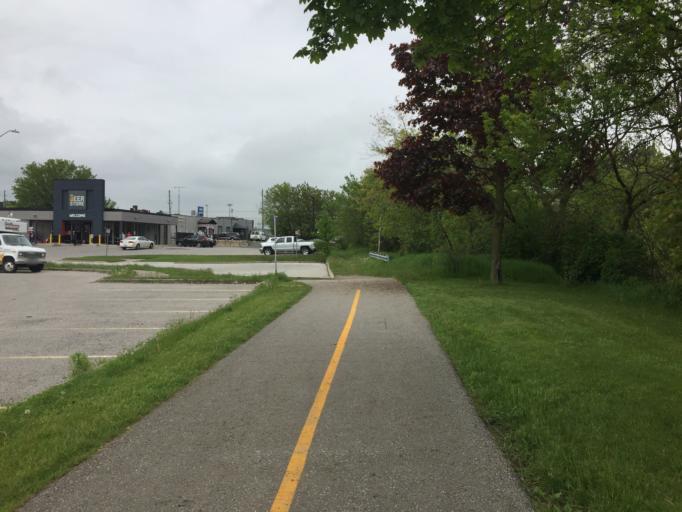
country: CA
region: Ontario
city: Oshawa
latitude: 43.8953
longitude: -78.8673
